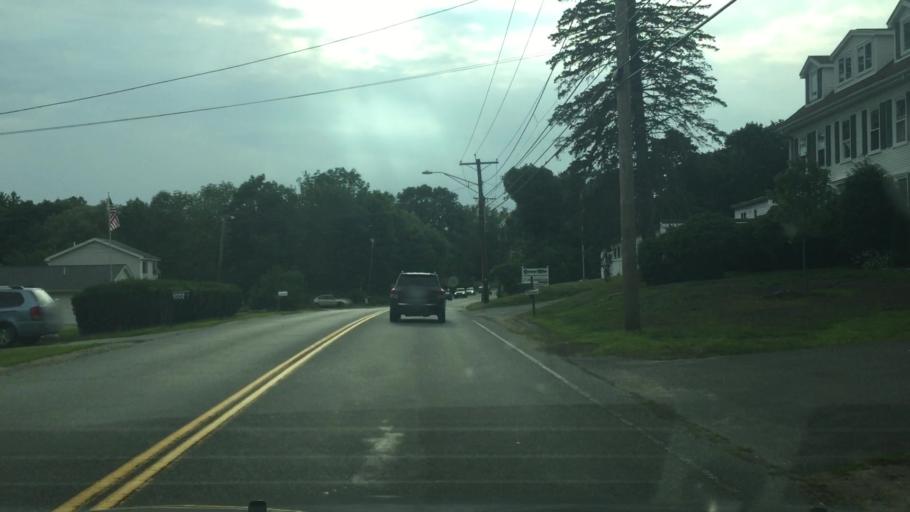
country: US
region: New Hampshire
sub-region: Rockingham County
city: Atkinson
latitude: 42.7897
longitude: -71.1456
